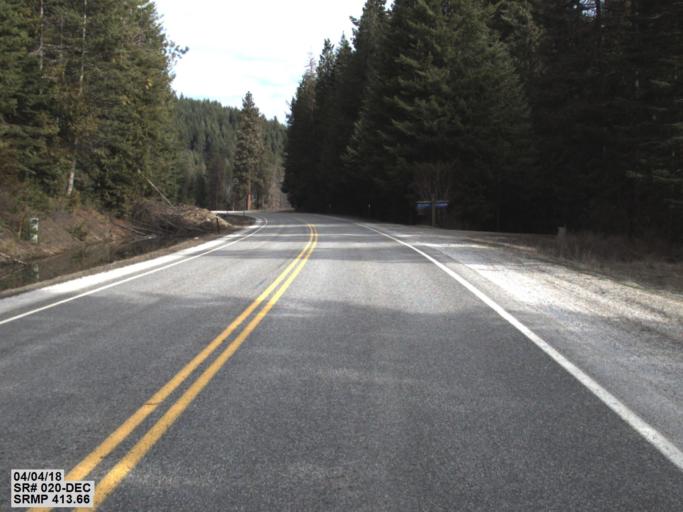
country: US
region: Washington
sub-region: Pend Oreille County
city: Newport
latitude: 48.4135
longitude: -117.3140
